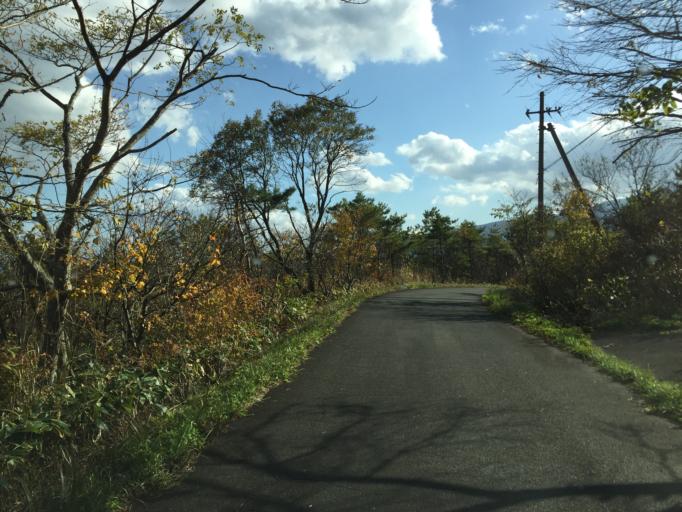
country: JP
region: Fukushima
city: Fukushima-shi
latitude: 37.7290
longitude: 140.3153
